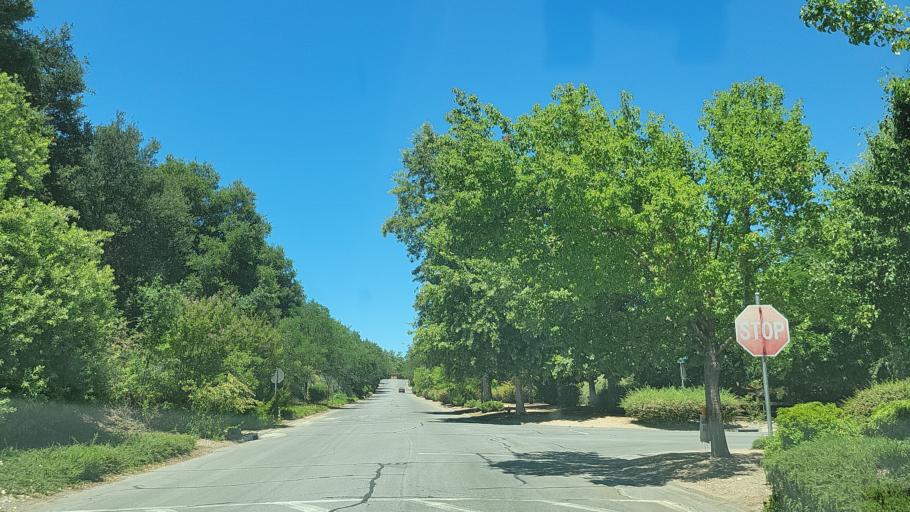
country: US
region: California
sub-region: San Luis Obispo County
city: Atascadero
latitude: 35.5140
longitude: -120.6753
